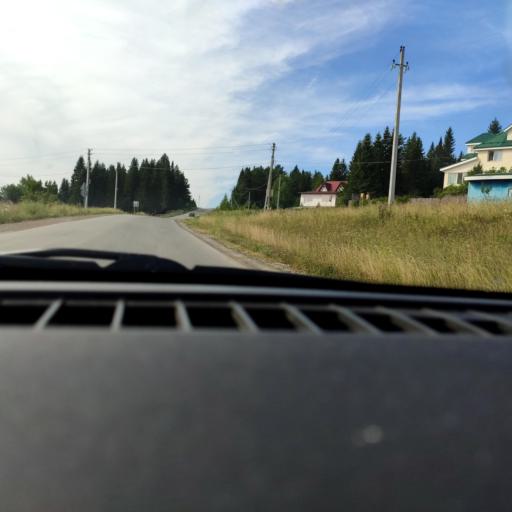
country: RU
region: Perm
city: Polazna
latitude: 58.3498
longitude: 56.2492
